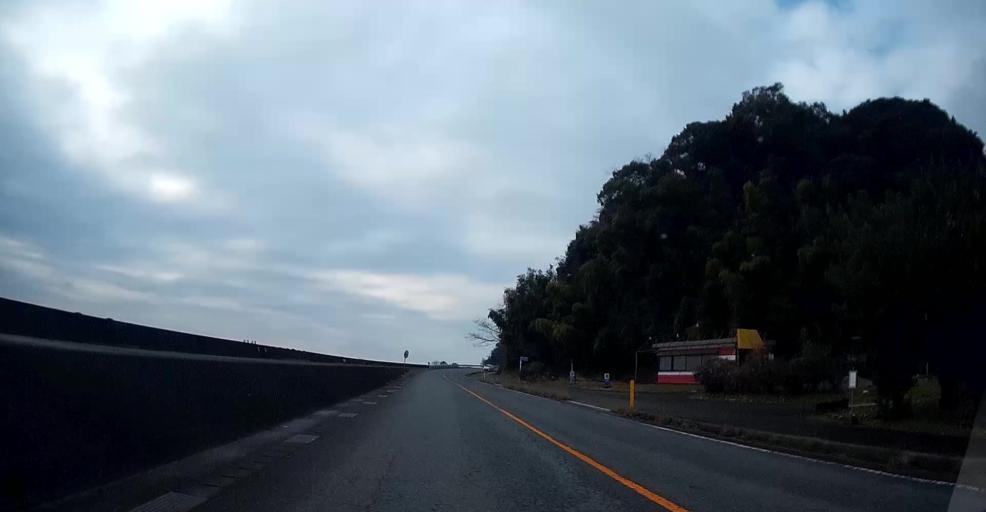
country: JP
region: Kumamoto
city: Matsubase
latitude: 32.6370
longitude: 130.6392
